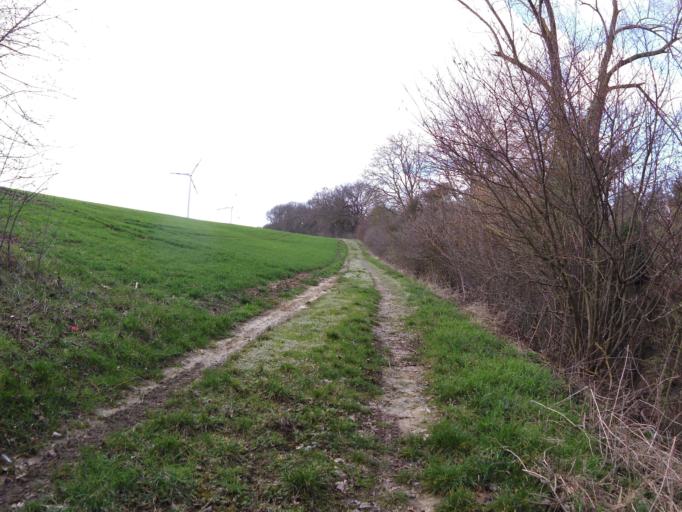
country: DE
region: Bavaria
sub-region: Regierungsbezirk Unterfranken
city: Buchbrunn
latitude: 49.7526
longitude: 10.1131
